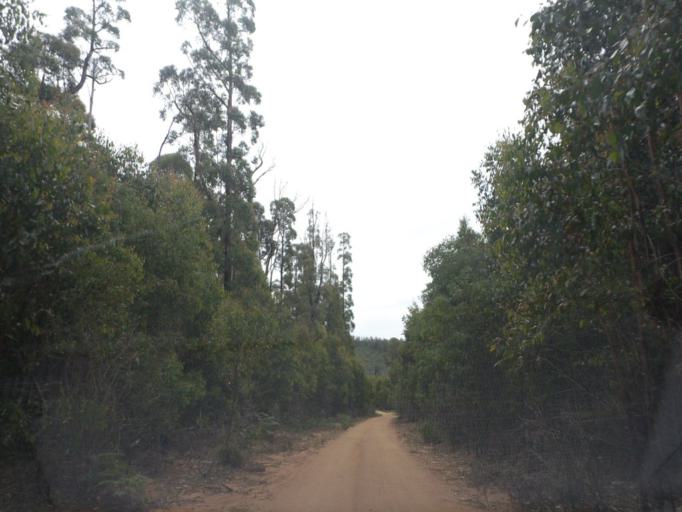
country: AU
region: Victoria
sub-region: Murrindindi
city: Alexandra
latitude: -37.3949
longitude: 145.5880
